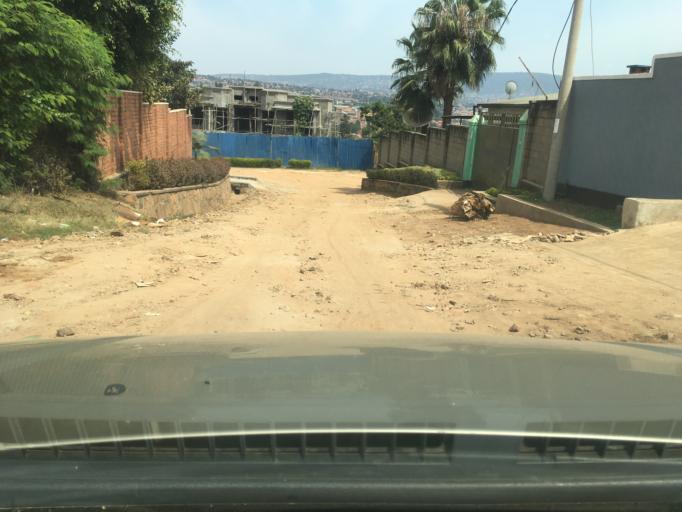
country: RW
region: Kigali
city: Kigali
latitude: -1.9657
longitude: 30.1014
